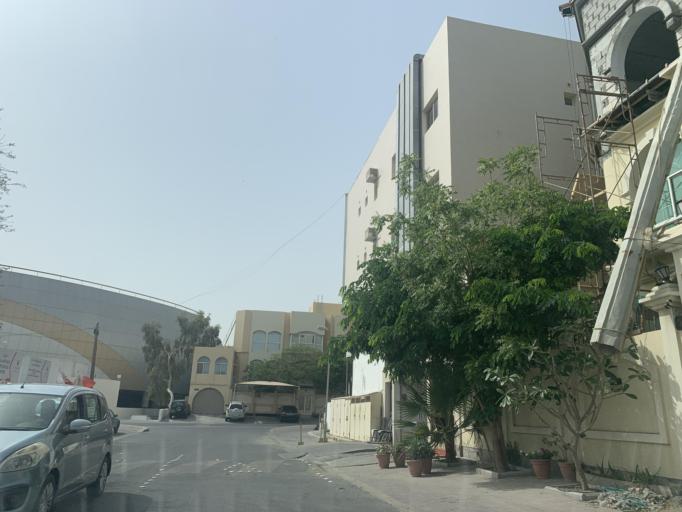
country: BH
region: Northern
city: Ar Rifa'
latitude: 26.1313
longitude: 50.5731
